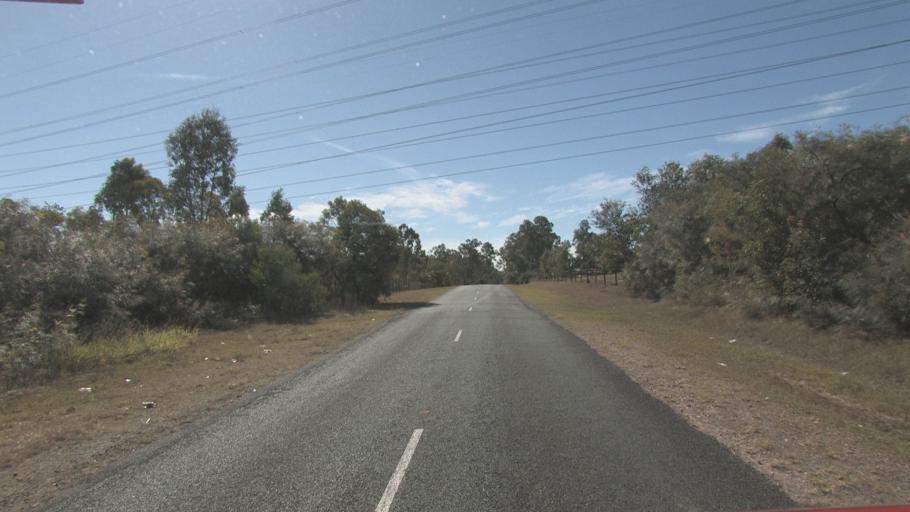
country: AU
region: Queensland
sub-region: Logan
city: North Maclean
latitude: -27.7336
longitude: 152.9606
